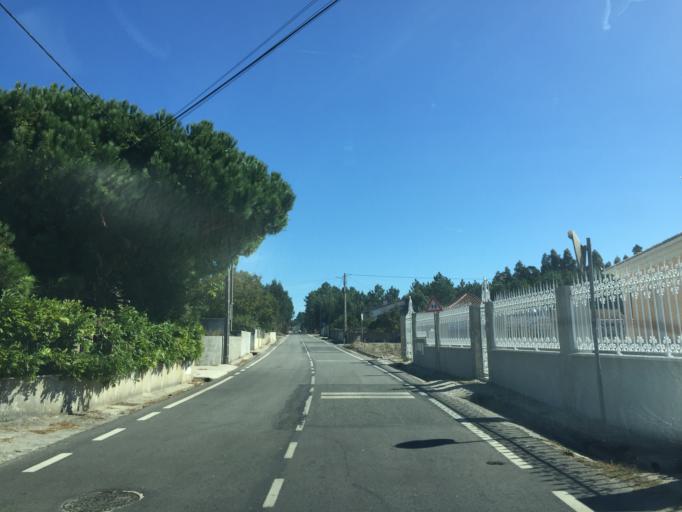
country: PT
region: Coimbra
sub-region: Figueira da Foz
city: Alhadas
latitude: 40.2198
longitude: -8.8169
